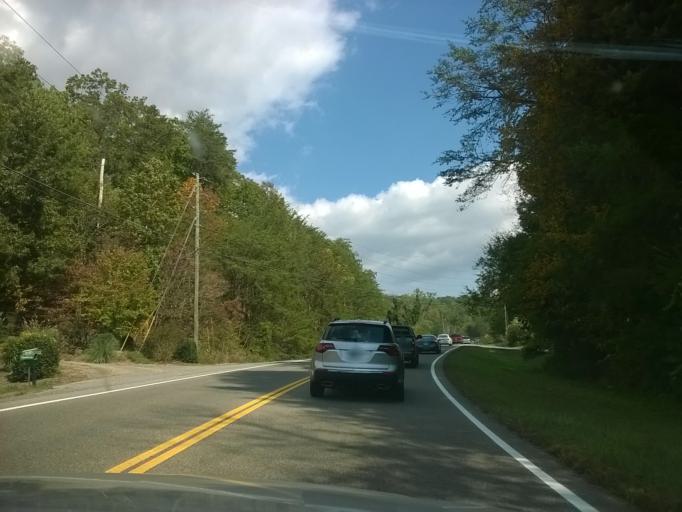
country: US
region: Tennessee
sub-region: Sevier County
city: Pigeon Forge
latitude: 35.7785
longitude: -83.6212
